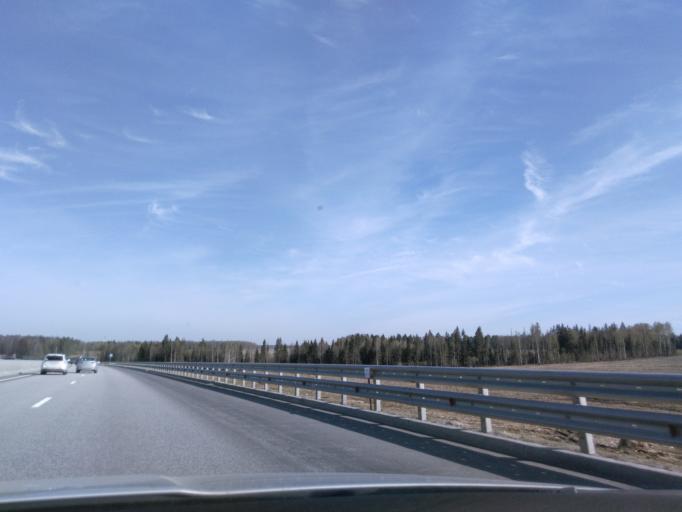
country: RU
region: Moskovskaya
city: Mendeleyevo
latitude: 56.0849
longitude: 37.2064
